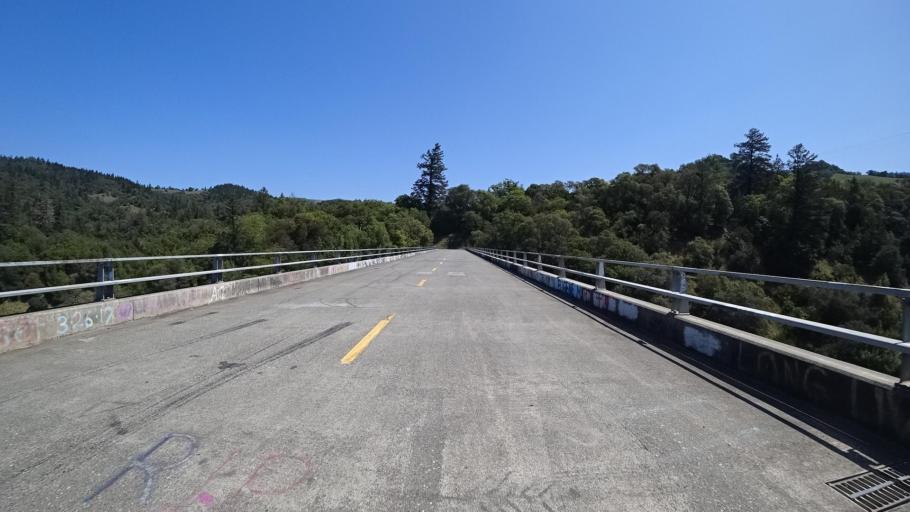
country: US
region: California
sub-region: Humboldt County
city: Redway
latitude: 40.1735
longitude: -123.6036
